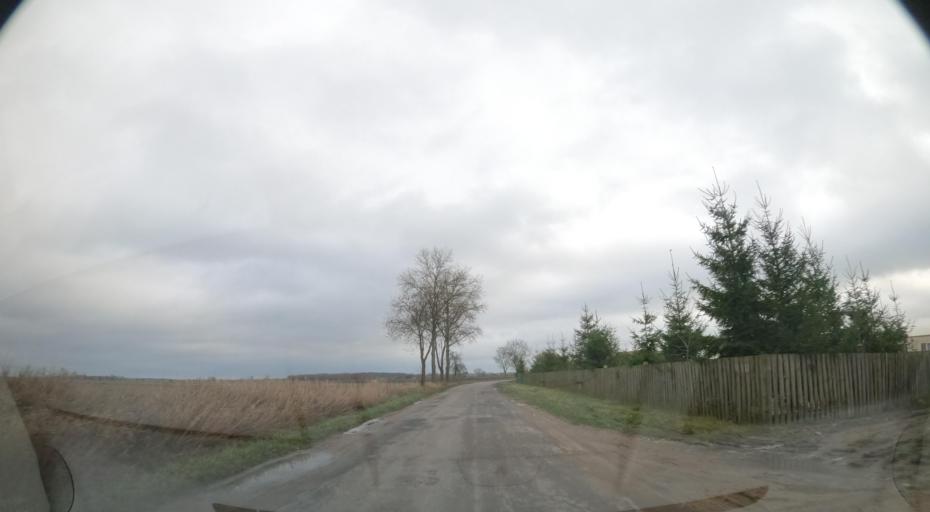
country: PL
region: Greater Poland Voivodeship
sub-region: Powiat pilski
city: Lobzenica
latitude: 53.2674
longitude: 17.2057
